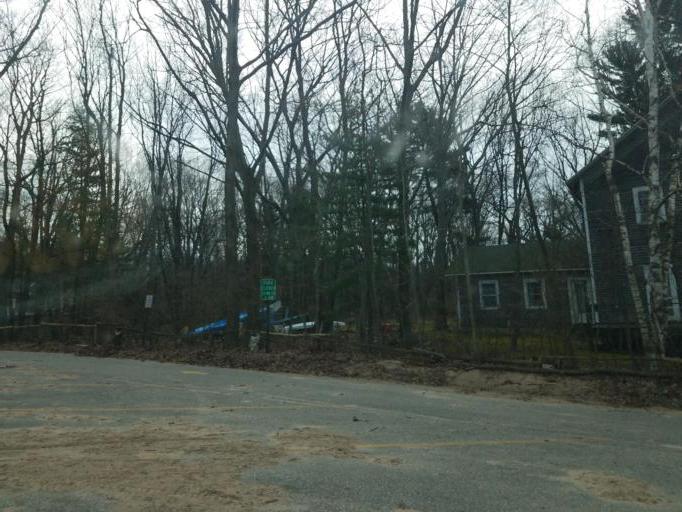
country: US
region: Michigan
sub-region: Oceana County
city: Hart
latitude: 43.6558
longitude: -86.5378
